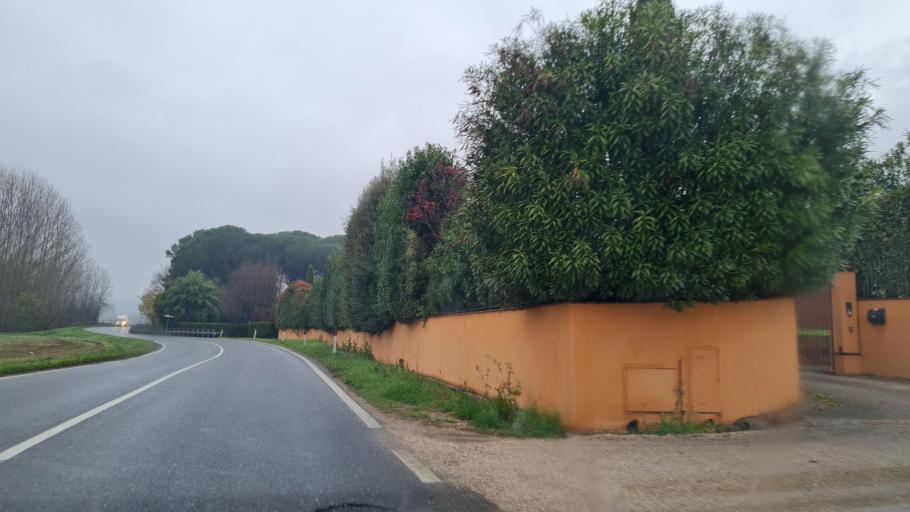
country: IT
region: Tuscany
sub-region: Provincia di Lucca
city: Lucca
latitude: 43.8592
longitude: 10.4581
